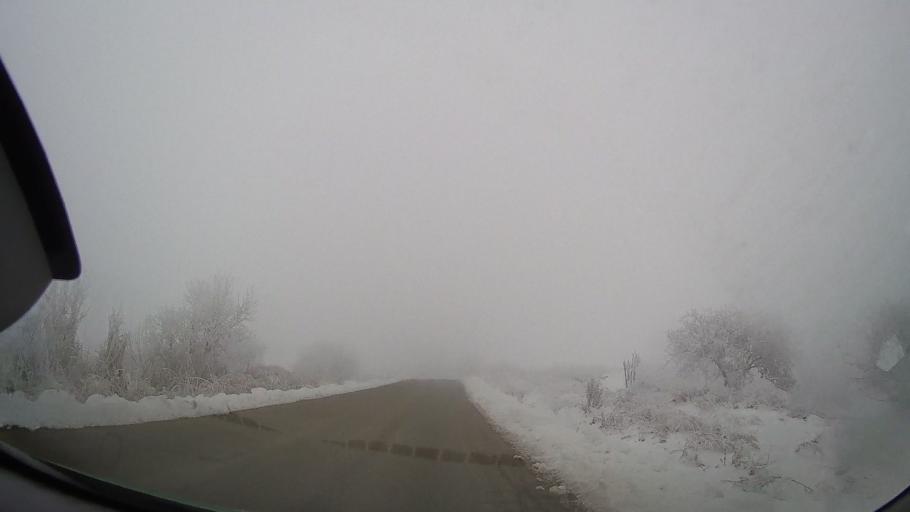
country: RO
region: Iasi
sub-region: Comuna Tansa
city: Suhulet
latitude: 46.8919
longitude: 27.2681
